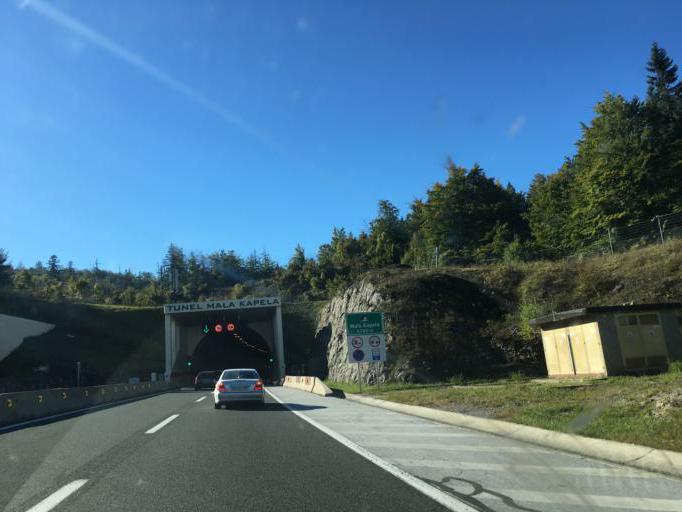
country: HR
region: Karlovacka
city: Ostarije
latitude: 45.1164
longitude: 15.2465
